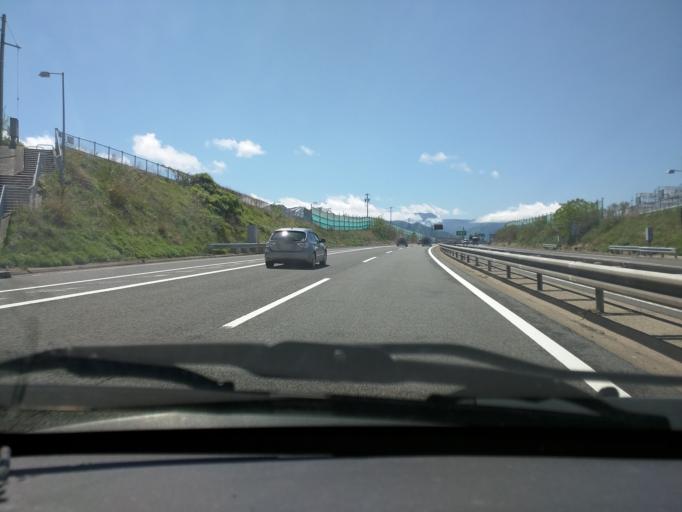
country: JP
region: Nagano
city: Nakano
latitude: 36.7371
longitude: 138.3178
